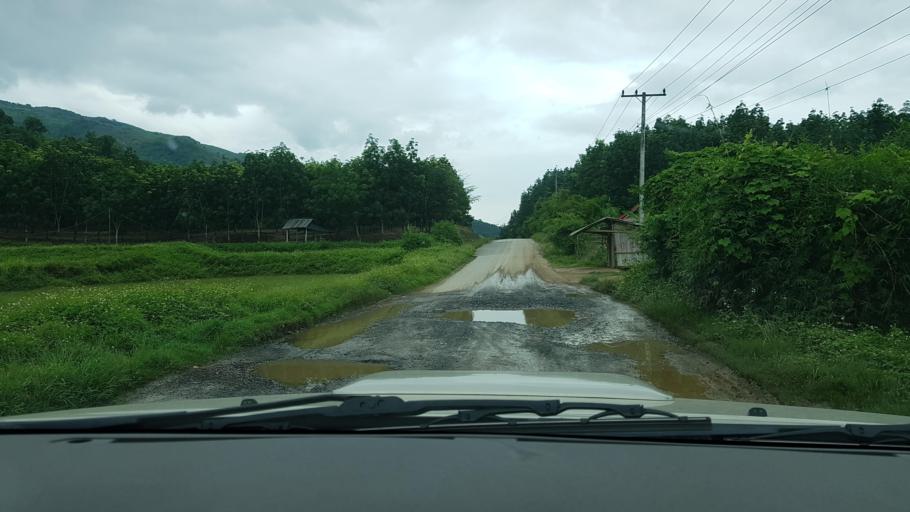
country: LA
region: Loungnamtha
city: Muang Nale
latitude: 20.2339
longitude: 101.5654
